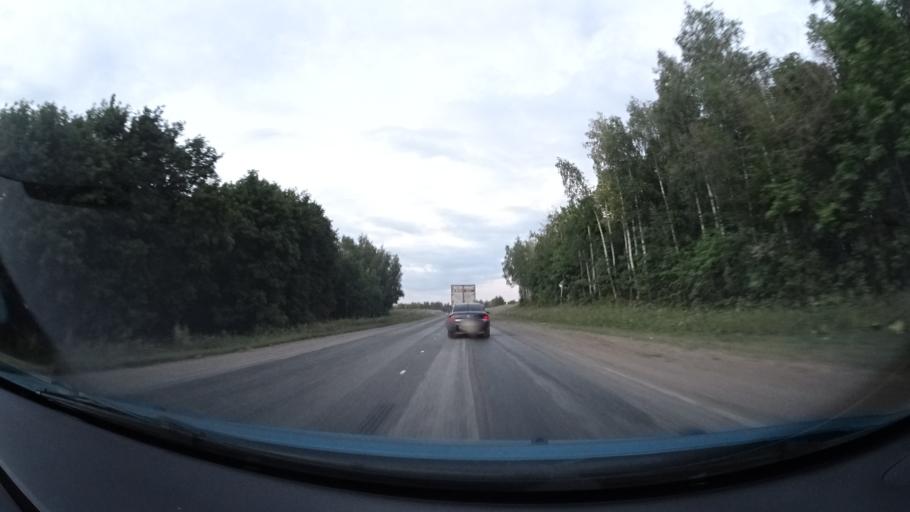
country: RU
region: Tatarstan
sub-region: Bugul'minskiy Rayon
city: Bugul'ma
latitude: 54.2674
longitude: 52.9587
